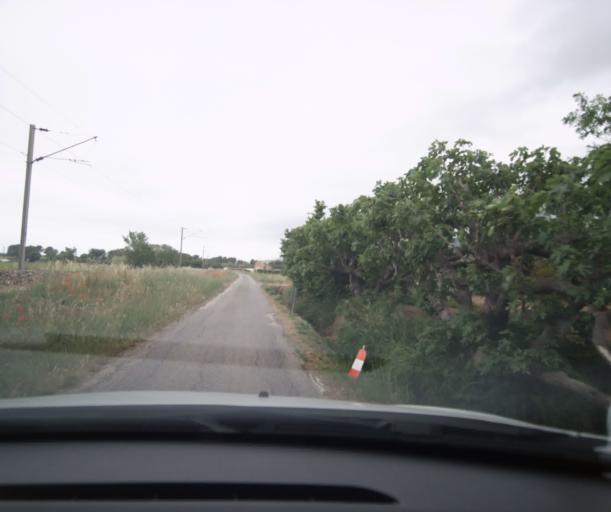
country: FR
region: Provence-Alpes-Cote d'Azur
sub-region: Departement du Var
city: La Farlede
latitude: 43.1442
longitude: 6.0473
